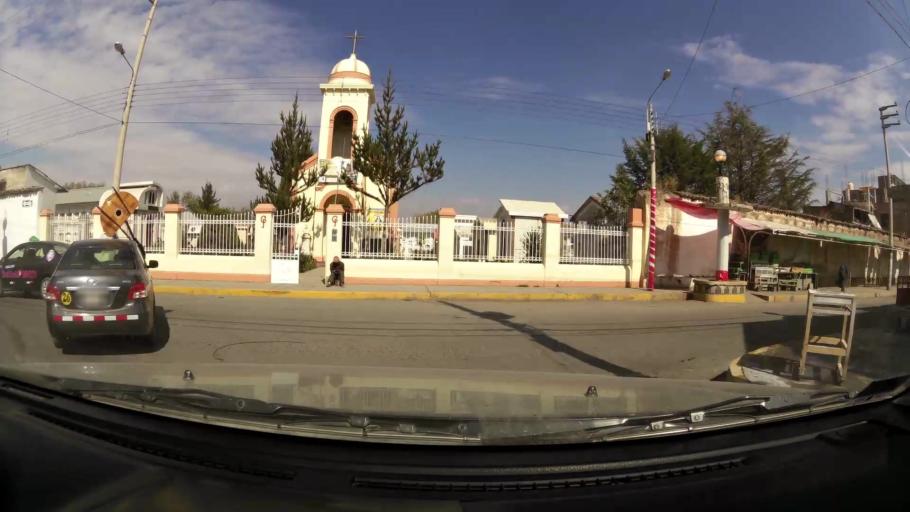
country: PE
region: Junin
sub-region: Provincia de Huancayo
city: El Tambo
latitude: -12.0722
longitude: -75.2168
